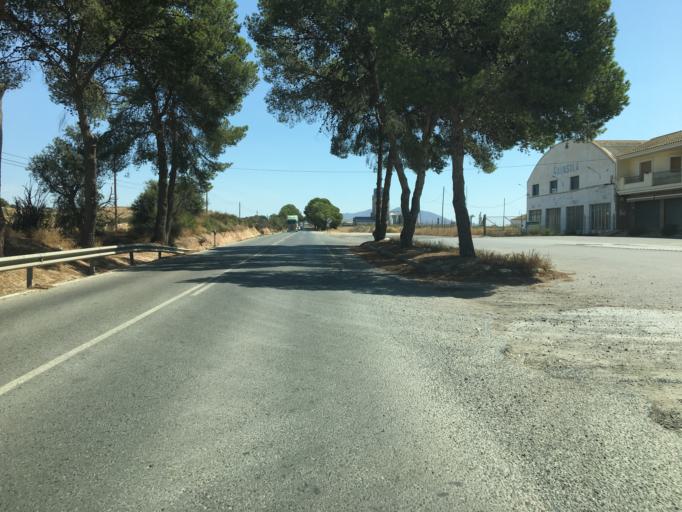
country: ES
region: Andalusia
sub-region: Provincia de Almeria
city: Huercal-Overa
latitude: 37.4111
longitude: -1.9303
